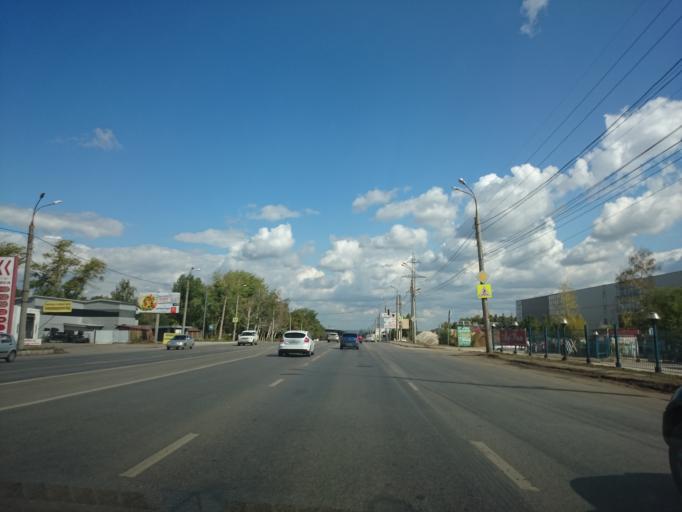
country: RU
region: Samara
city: Samara
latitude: 53.2633
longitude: 50.2433
